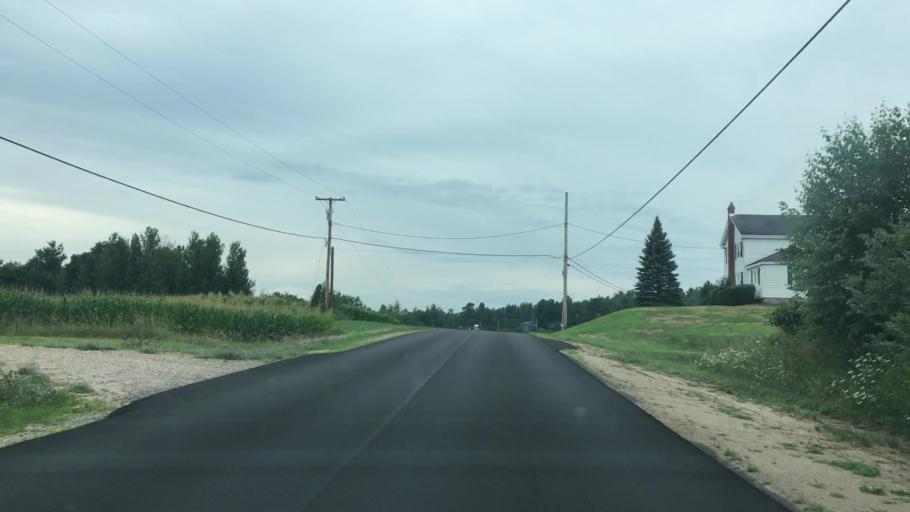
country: US
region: New York
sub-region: Clinton County
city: Peru
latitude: 44.5732
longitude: -73.5701
